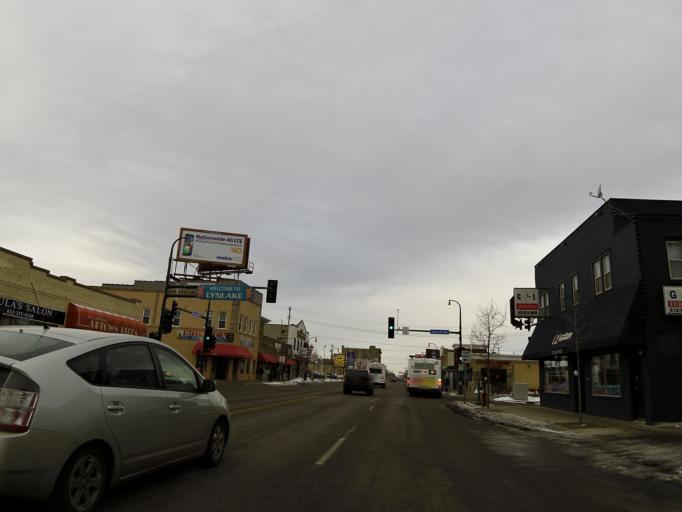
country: US
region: Minnesota
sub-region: Hennepin County
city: Minneapolis
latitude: 44.9484
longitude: -93.2837
